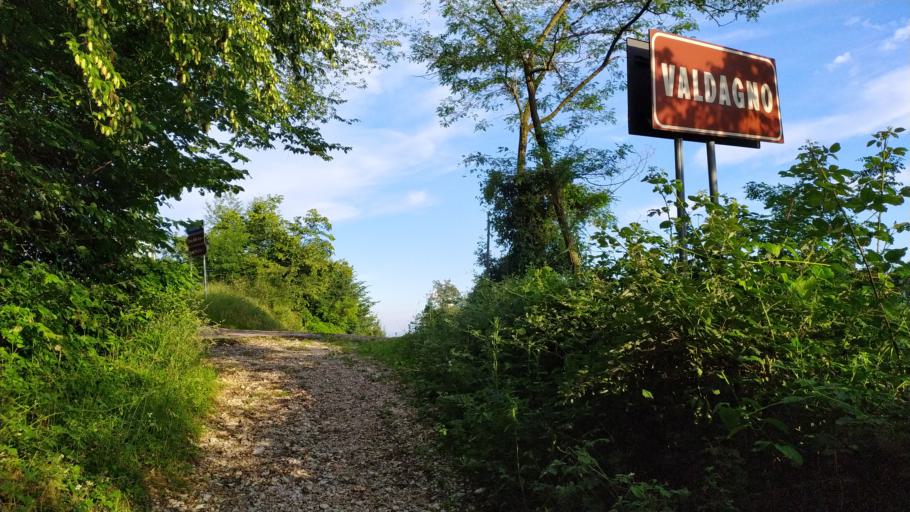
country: IT
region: Veneto
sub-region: Provincia di Vicenza
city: San Quirico
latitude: 45.6804
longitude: 11.2787
